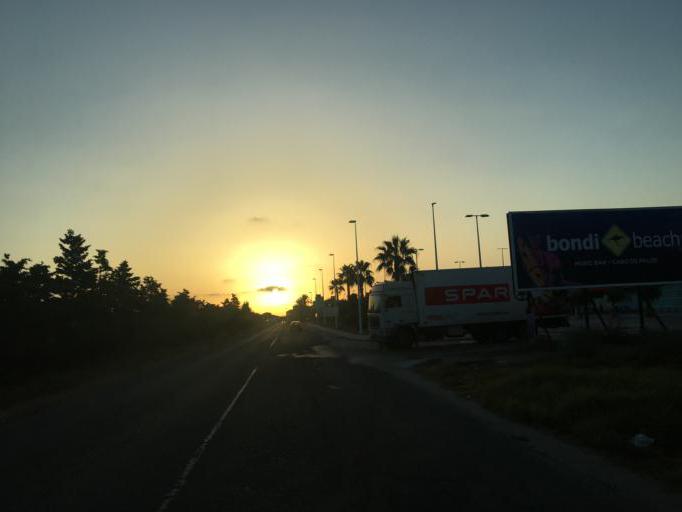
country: ES
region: Murcia
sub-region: Murcia
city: La Manga del Mar Menor
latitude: 37.6279
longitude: -0.7118
